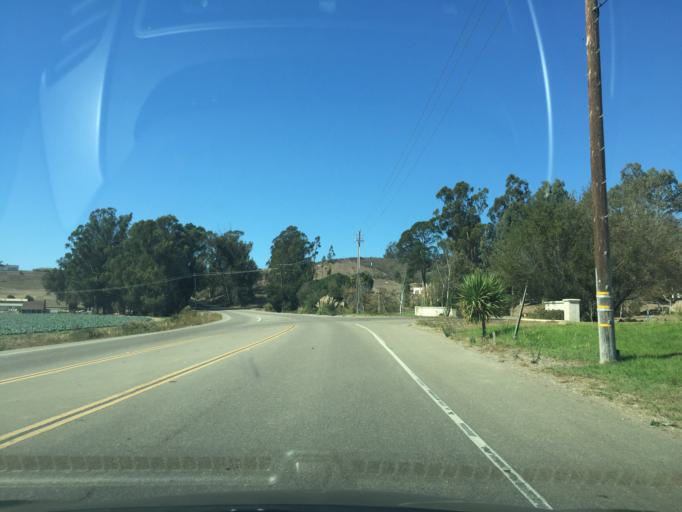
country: US
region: California
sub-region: Santa Barbara County
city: Mission Hills
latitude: 34.6767
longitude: -120.4456
